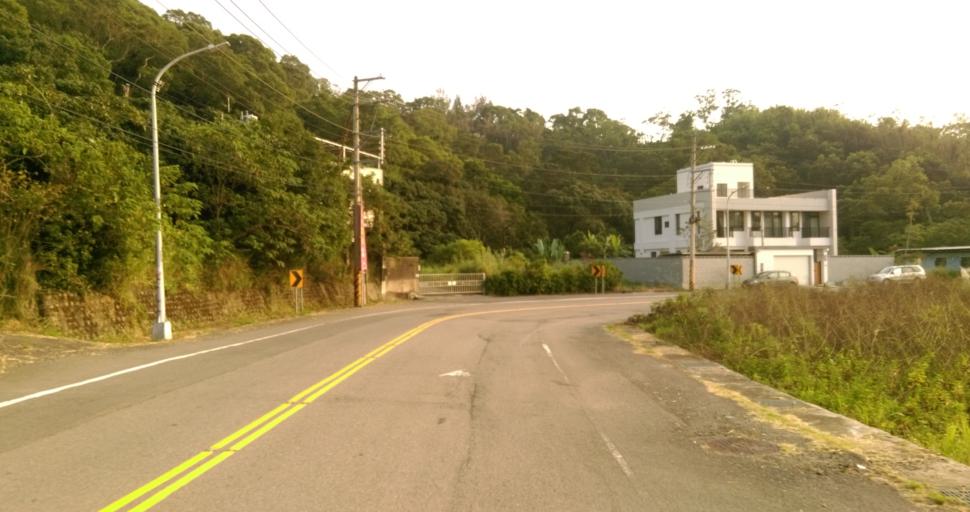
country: TW
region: Taiwan
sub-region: Hsinchu
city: Hsinchu
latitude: 24.7559
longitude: 120.9428
